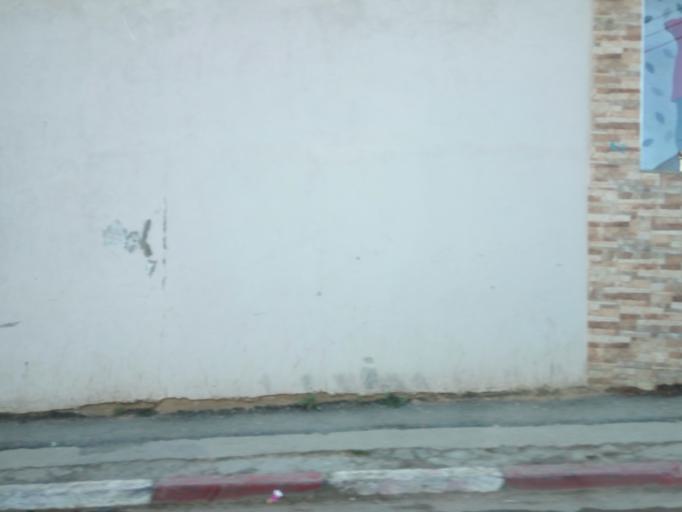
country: DZ
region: Tipaza
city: Saoula
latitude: 36.7184
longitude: 3.0118
